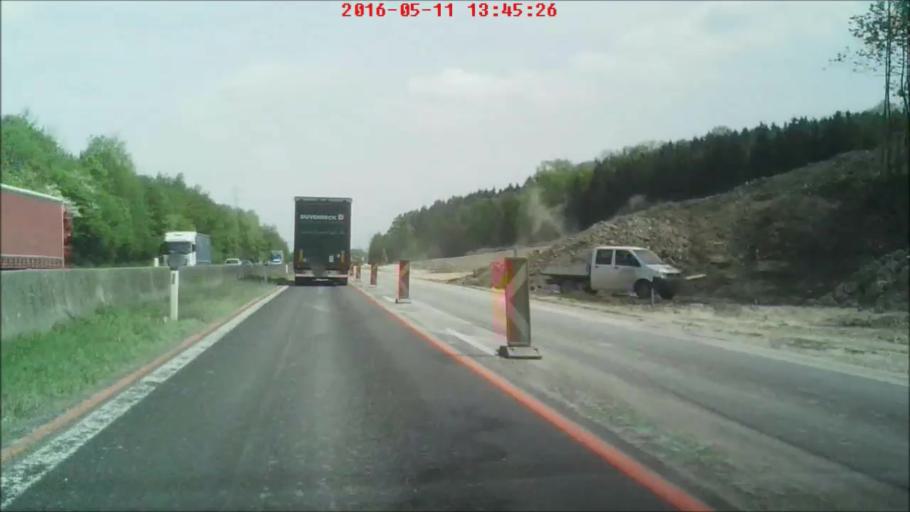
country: AT
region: Upper Austria
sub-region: Politischer Bezirk Vocklabruck
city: Wolfsegg am Hausruck
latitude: 48.2177
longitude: 13.6205
